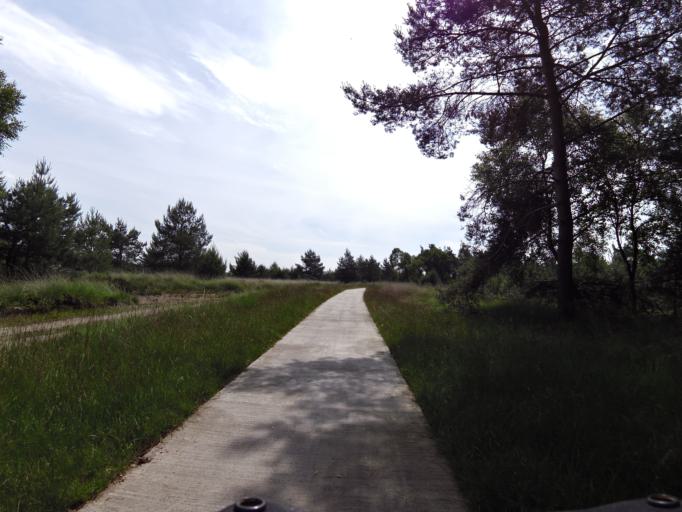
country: NL
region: Gelderland
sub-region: Gemeente Rozendaal
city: Rozendaal
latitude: 52.0471
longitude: 5.9825
